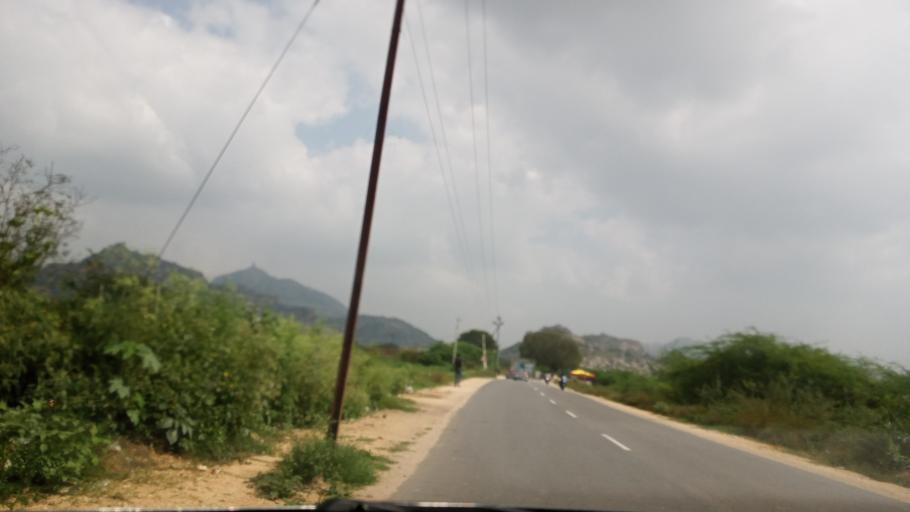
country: IN
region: Andhra Pradesh
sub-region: Chittoor
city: Madanapalle
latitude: 13.6423
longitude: 78.5571
